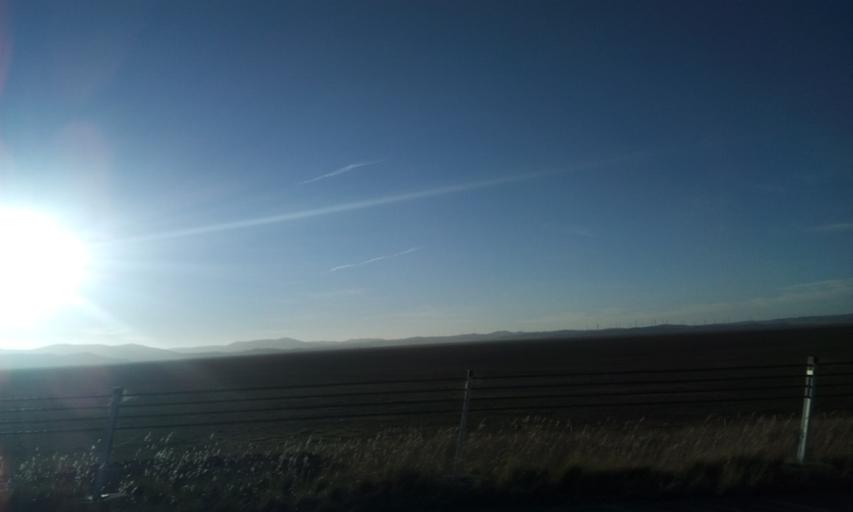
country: AU
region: New South Wales
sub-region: Yass Valley
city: Gundaroo
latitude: -35.0452
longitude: 149.3768
